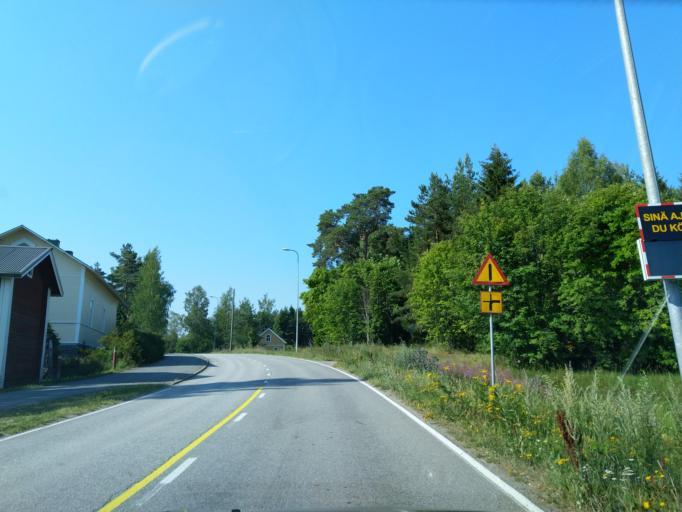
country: FI
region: Satakunta
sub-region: Pori
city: Pomarkku
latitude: 61.6908
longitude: 22.0047
